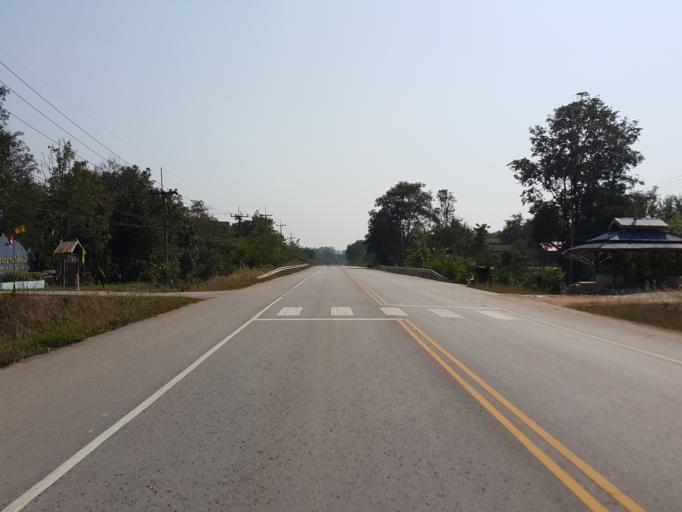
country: TH
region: Lampang
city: Mueang Pan
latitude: 18.9326
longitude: 99.6114
